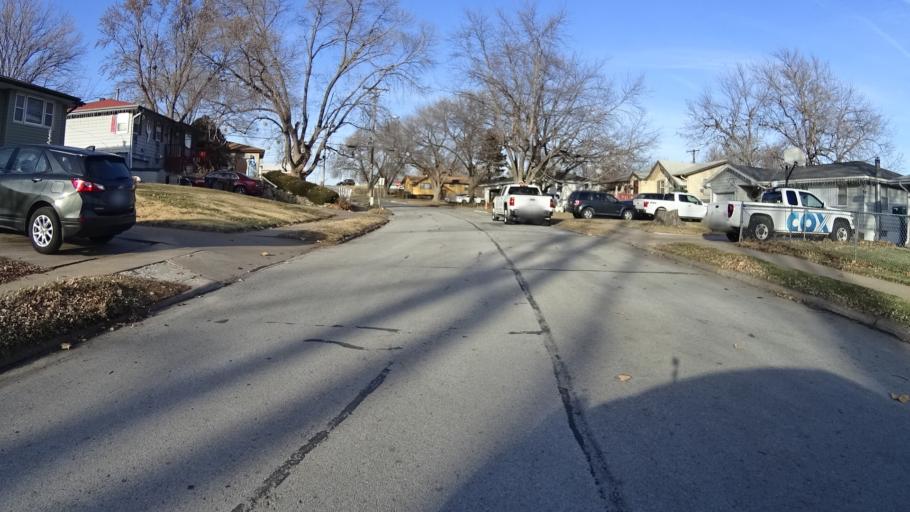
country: US
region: Nebraska
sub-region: Sarpy County
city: La Vista
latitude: 41.1879
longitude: -95.9947
